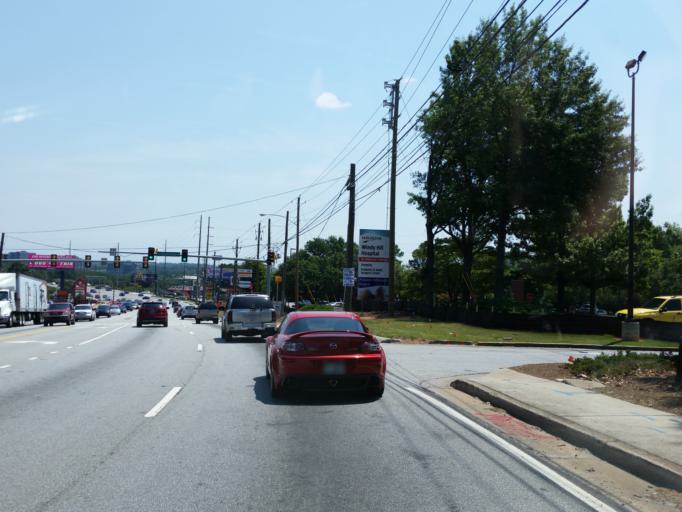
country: US
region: Georgia
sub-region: Cobb County
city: Smyrna
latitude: 33.9012
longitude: -84.4795
